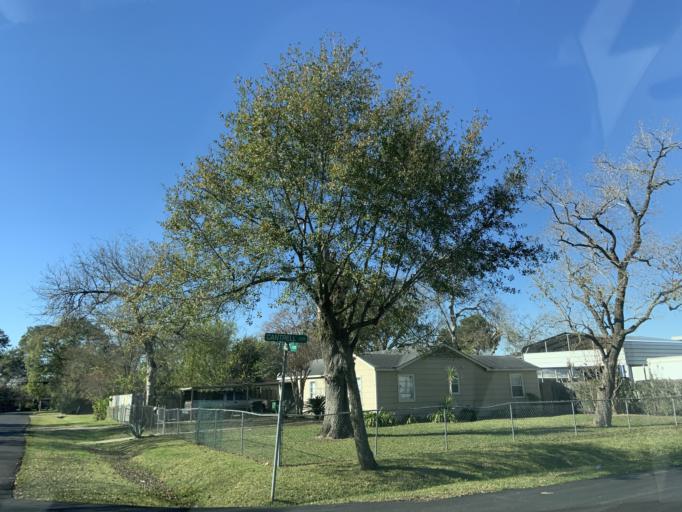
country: US
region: Texas
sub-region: Harris County
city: Bellaire
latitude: 29.6896
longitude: -95.4994
